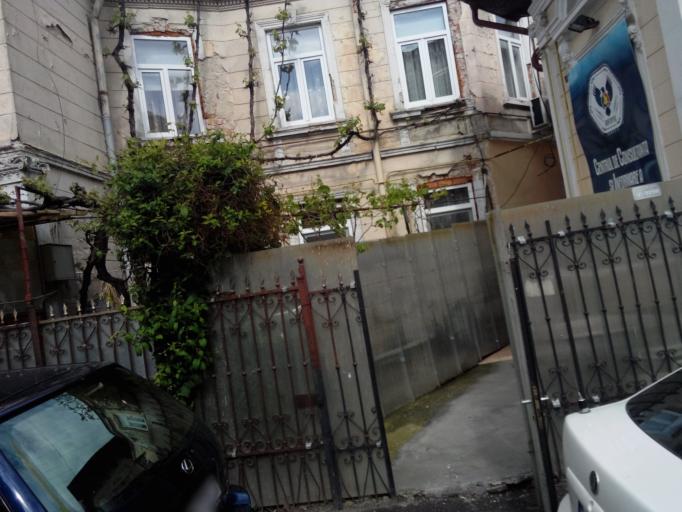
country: RO
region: Bucuresti
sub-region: Municipiul Bucuresti
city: Bucuresti
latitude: 44.4226
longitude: 26.0997
